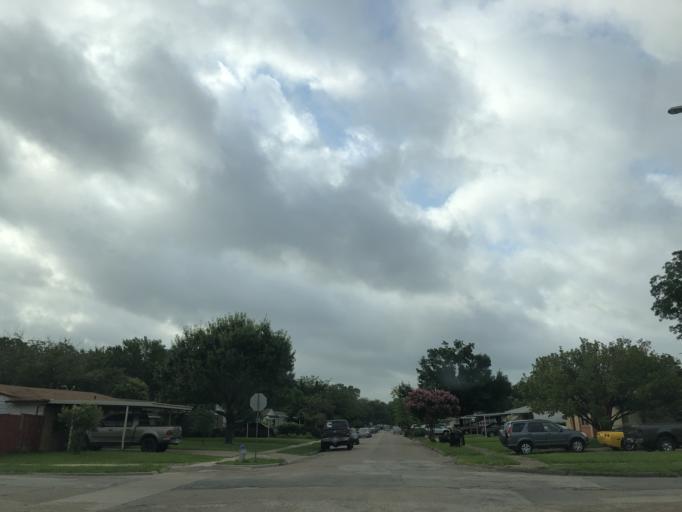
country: US
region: Texas
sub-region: Dallas County
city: Mesquite
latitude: 32.8322
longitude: -96.6422
